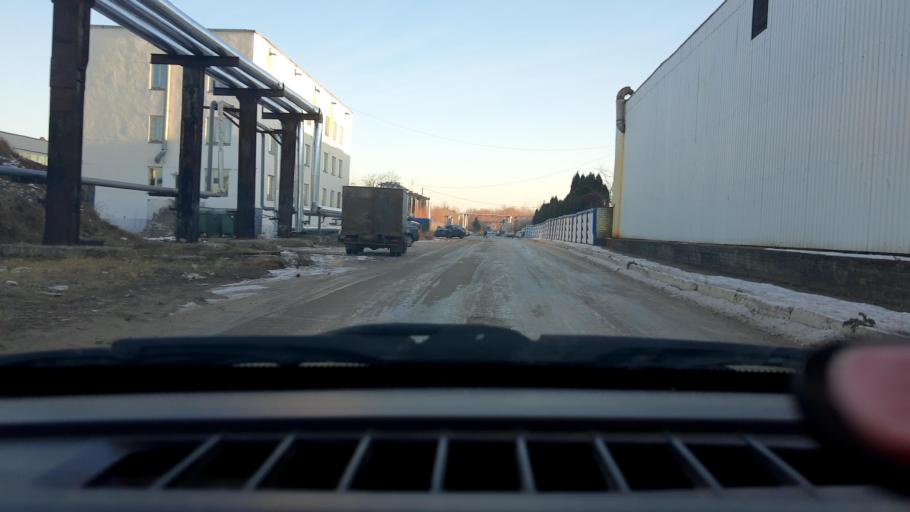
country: RU
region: Nizjnij Novgorod
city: Gorbatovka
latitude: 56.2744
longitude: 43.8360
